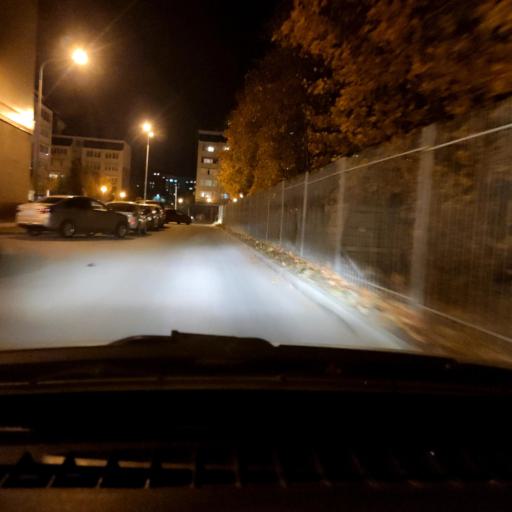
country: RU
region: Samara
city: Tol'yatti
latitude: 53.5463
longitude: 49.3132
